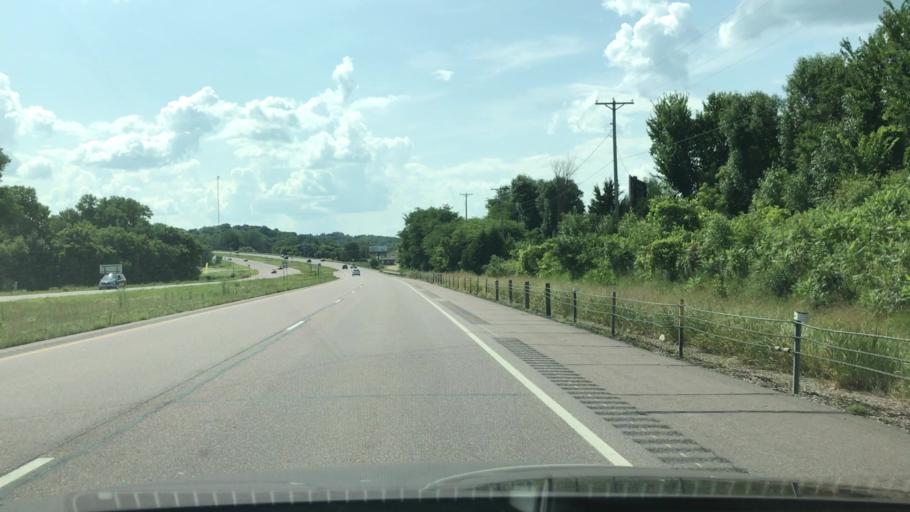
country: US
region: Minnesota
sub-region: Nicollet County
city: North Mankato
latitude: 44.1526
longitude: -94.0660
